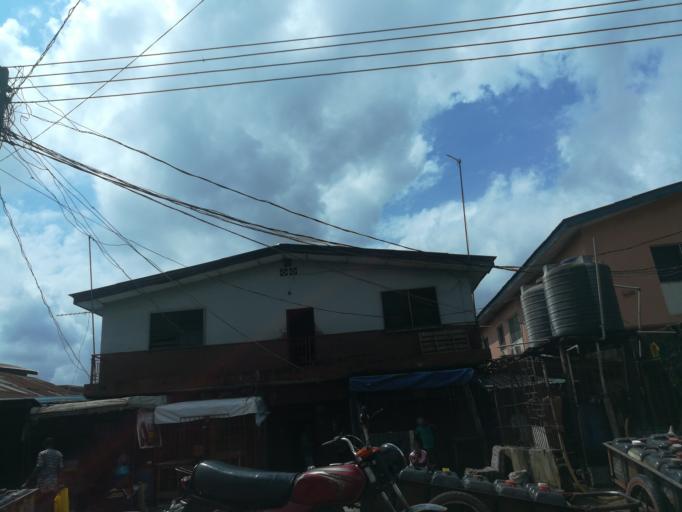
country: NG
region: Lagos
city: Mushin
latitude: 6.5353
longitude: 3.3623
